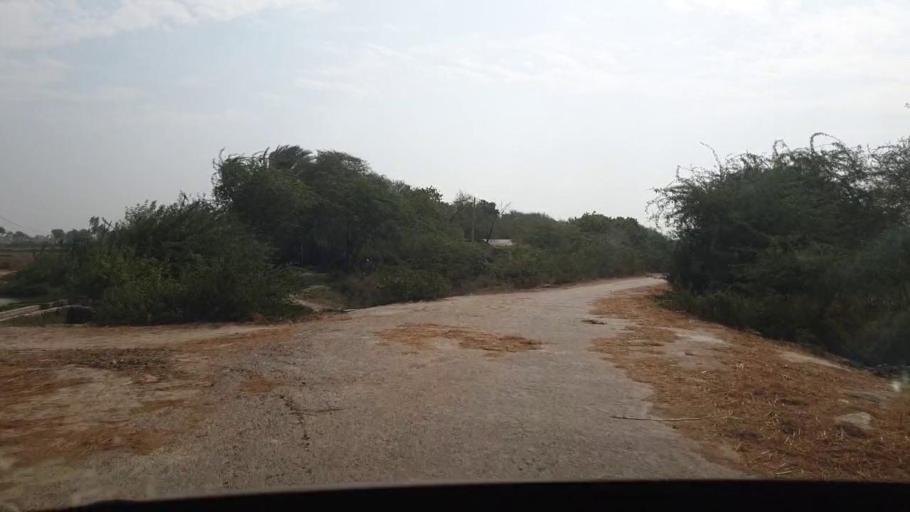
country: PK
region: Sindh
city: Chuhar Jamali
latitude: 24.3192
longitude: 67.9443
